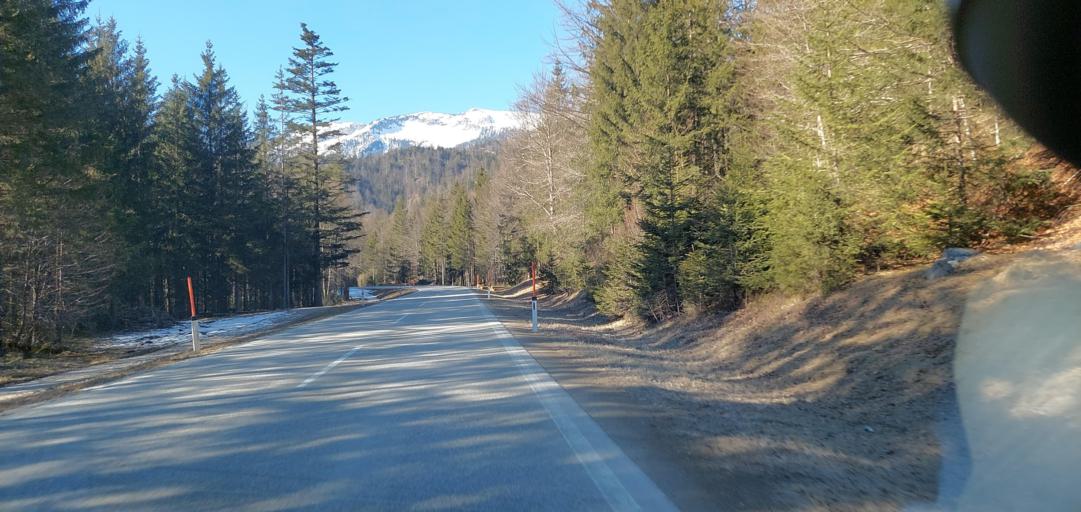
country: AT
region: Upper Austria
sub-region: Politischer Bezirk Gmunden
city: Bad Ischl
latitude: 47.7745
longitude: 13.6167
